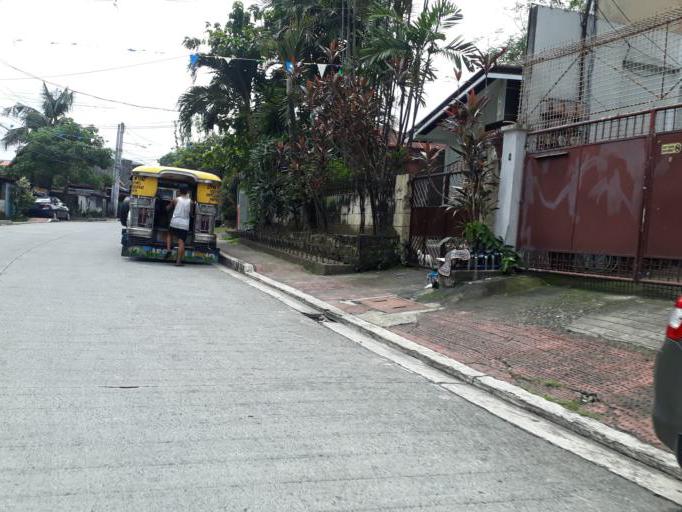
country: PH
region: Calabarzon
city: Bagong Pagasa
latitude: 14.6652
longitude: 121.0342
